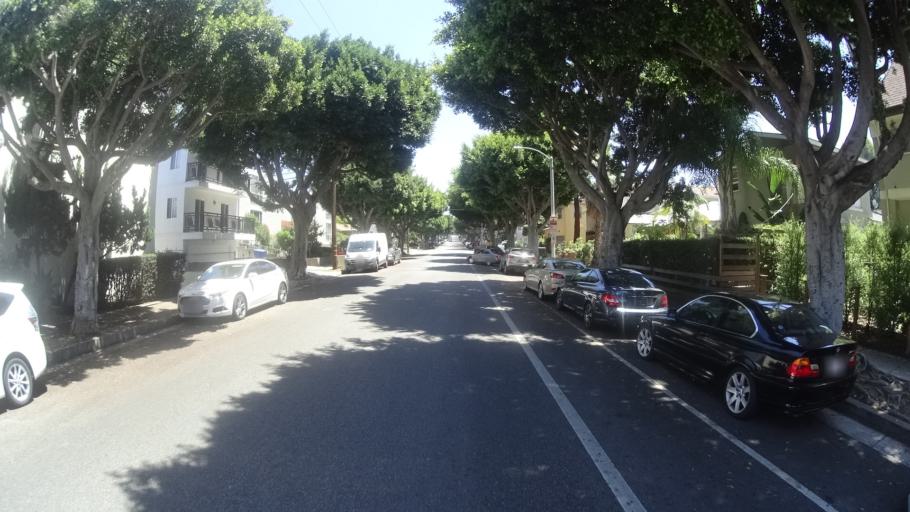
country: US
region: California
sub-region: Los Angeles County
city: Santa Monica
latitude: 34.0356
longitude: -118.4748
